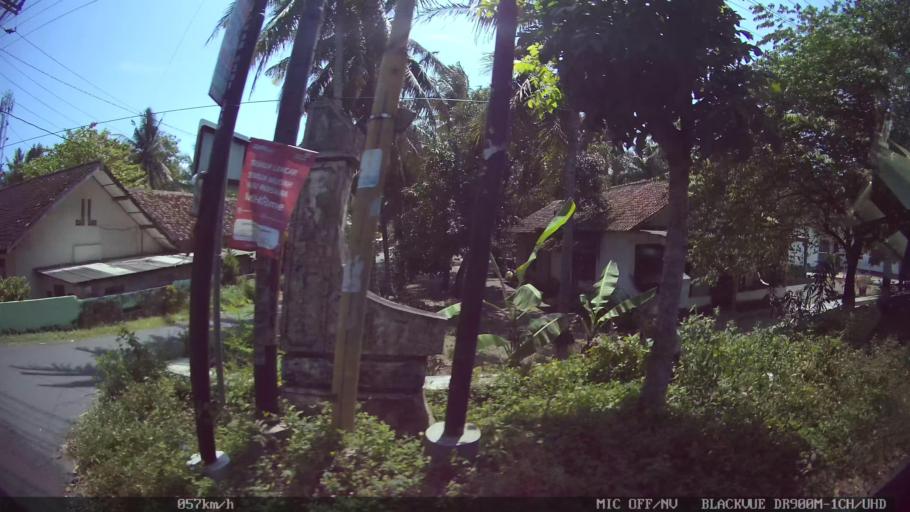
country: ID
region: Daerah Istimewa Yogyakarta
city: Srandakan
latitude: -7.9137
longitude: 110.0949
